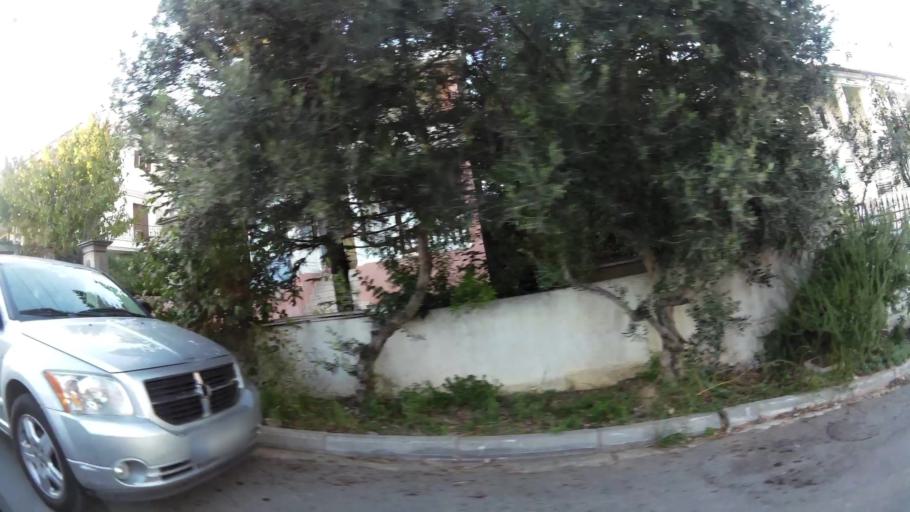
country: GR
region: Attica
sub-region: Nomarchia Anatolikis Attikis
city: Kryoneri
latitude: 38.1463
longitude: 23.8309
